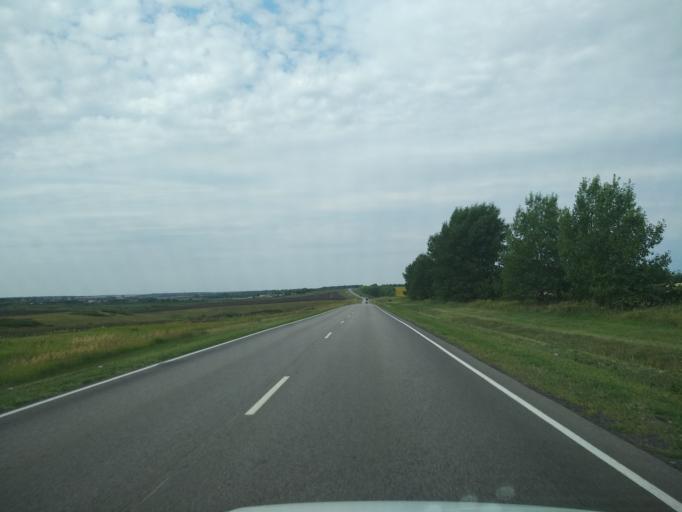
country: RU
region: Voronezj
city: Pereleshinskiy
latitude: 51.8595
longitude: 40.3507
